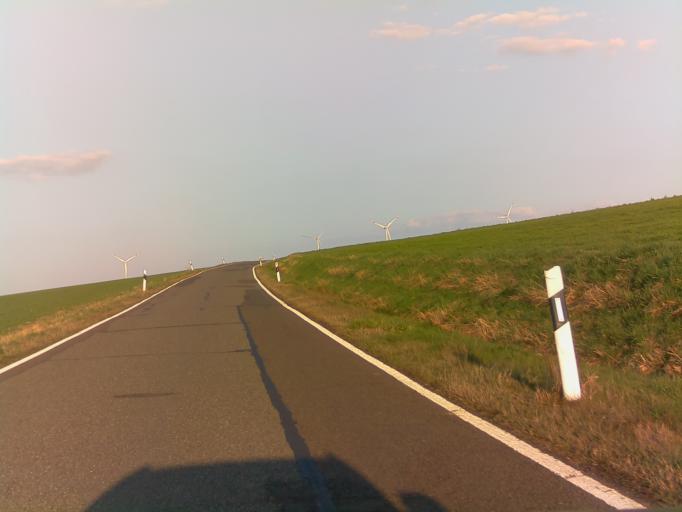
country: DE
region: Rheinland-Pfalz
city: Oberhausen an der Appel
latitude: 49.7324
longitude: 7.8573
